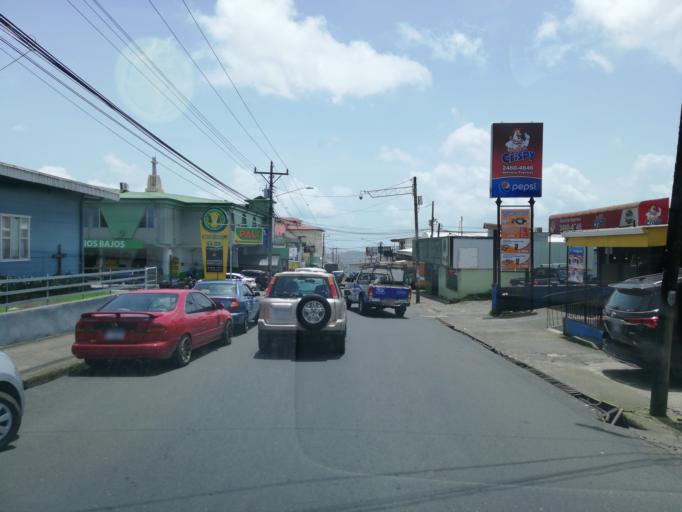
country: CR
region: Alajuela
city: Quesada
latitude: 10.3217
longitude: -84.4296
